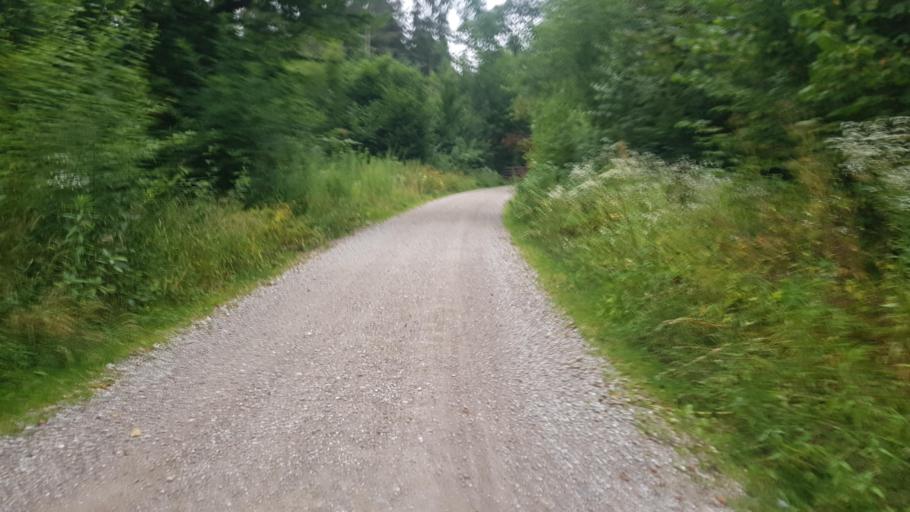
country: DE
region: Bavaria
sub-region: Upper Bavaria
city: Gauting
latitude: 48.0526
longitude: 11.3586
